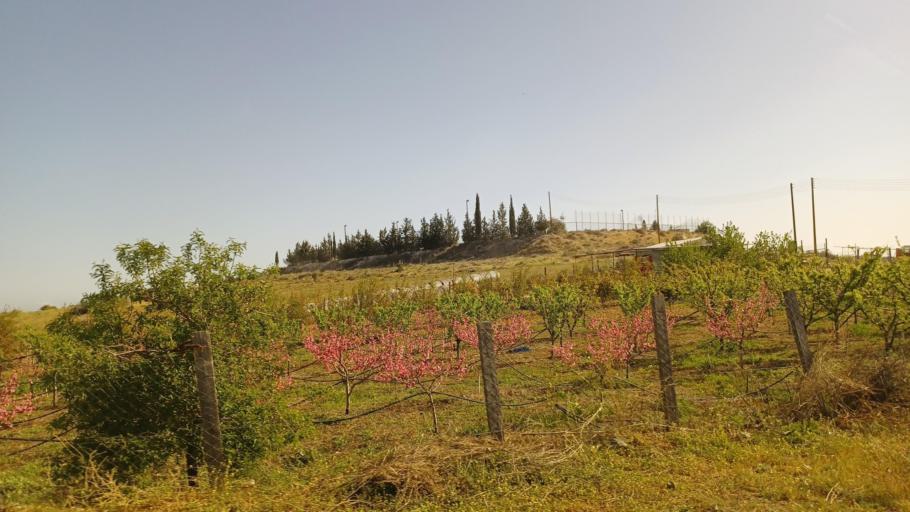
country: CY
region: Lefkosia
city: Astromeritis
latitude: 35.0779
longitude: 33.0207
